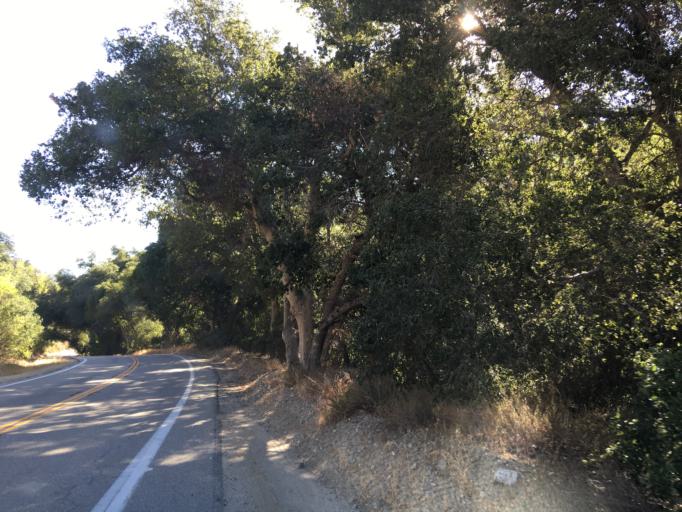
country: US
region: California
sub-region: Los Angeles County
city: Green Valley
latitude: 34.6223
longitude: -118.5566
